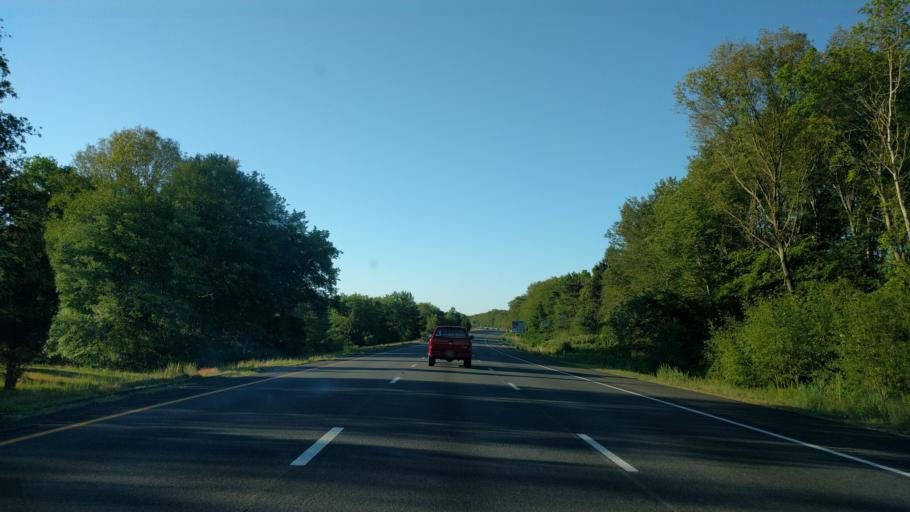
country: US
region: Massachusetts
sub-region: Norfolk County
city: Bellingham
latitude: 42.1262
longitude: -71.4739
